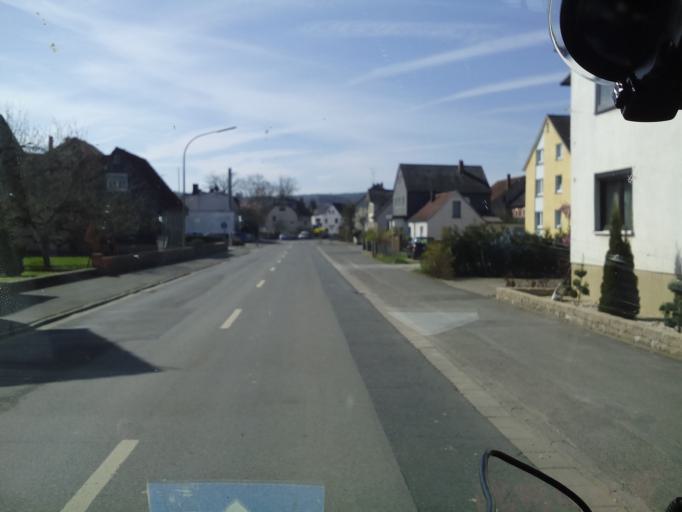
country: DE
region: Bavaria
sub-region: Upper Franconia
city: Michelau
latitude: 50.1664
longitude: 11.1133
